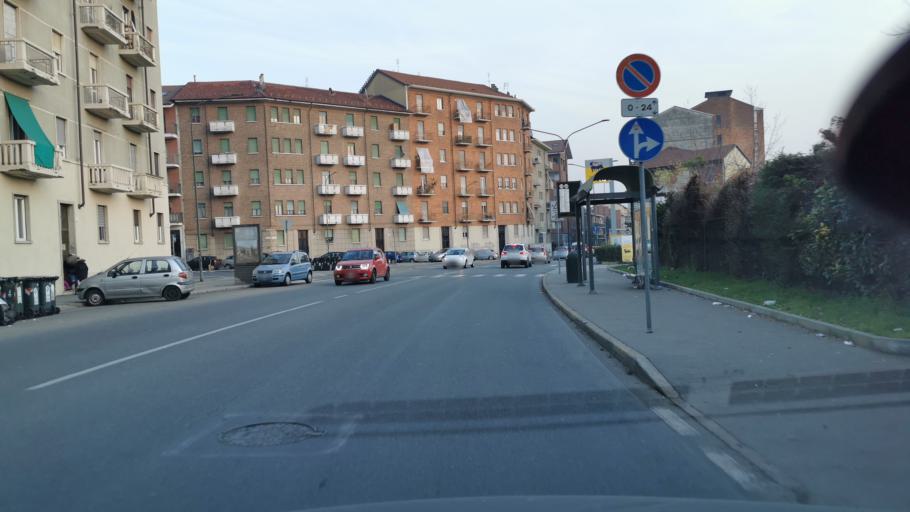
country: IT
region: Piedmont
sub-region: Provincia di Torino
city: Venaria Reale
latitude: 45.0944
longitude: 7.6502
